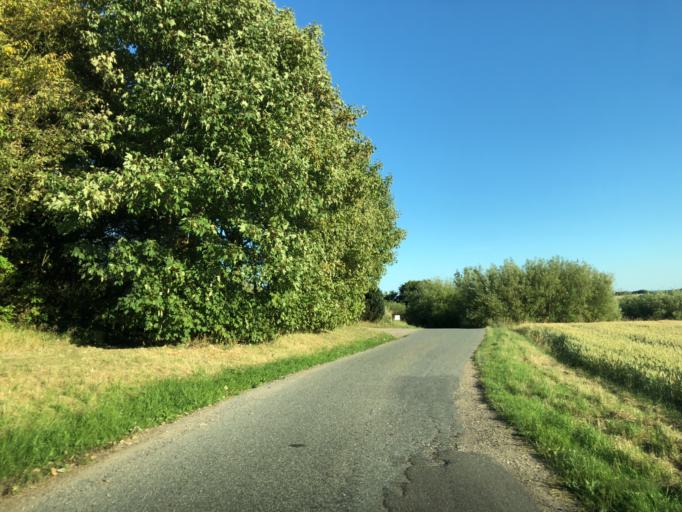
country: DK
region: Central Jutland
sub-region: Skanderborg Kommune
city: Ry
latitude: 55.9794
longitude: 9.7994
